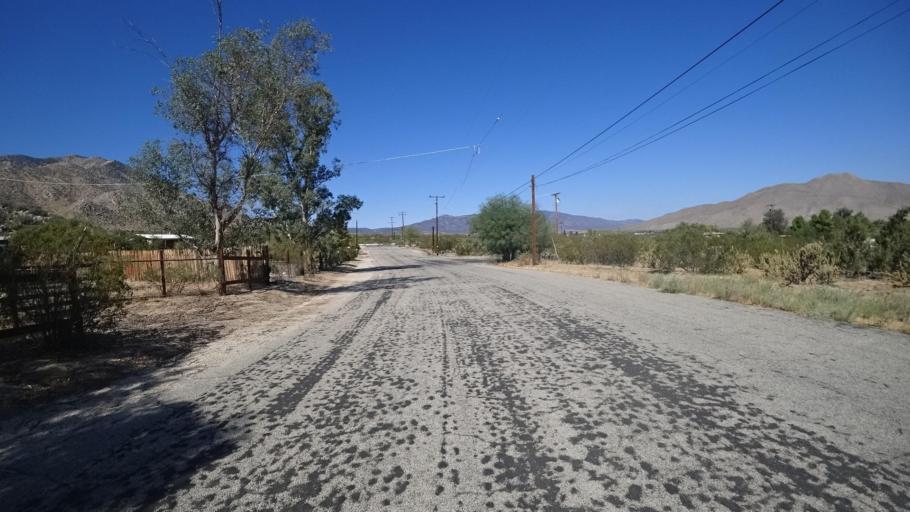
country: US
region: California
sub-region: San Diego County
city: Julian
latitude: 33.0746
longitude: -116.4439
